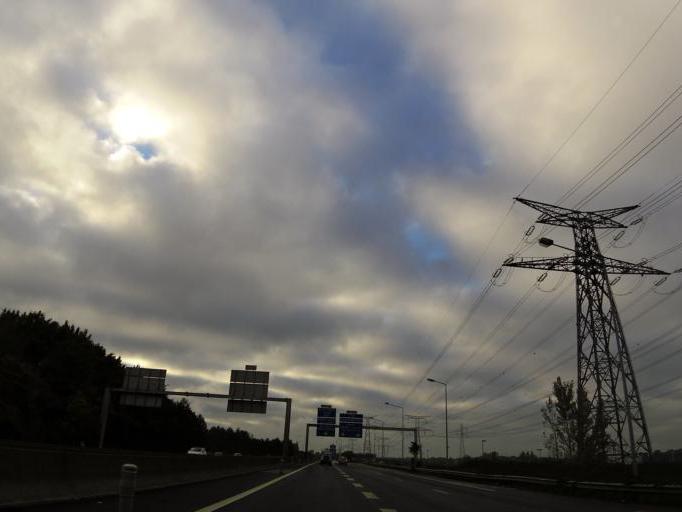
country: FR
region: Ile-de-France
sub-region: Departement de Seine-et-Marne
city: Collegien
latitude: 48.8365
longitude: 2.6649
